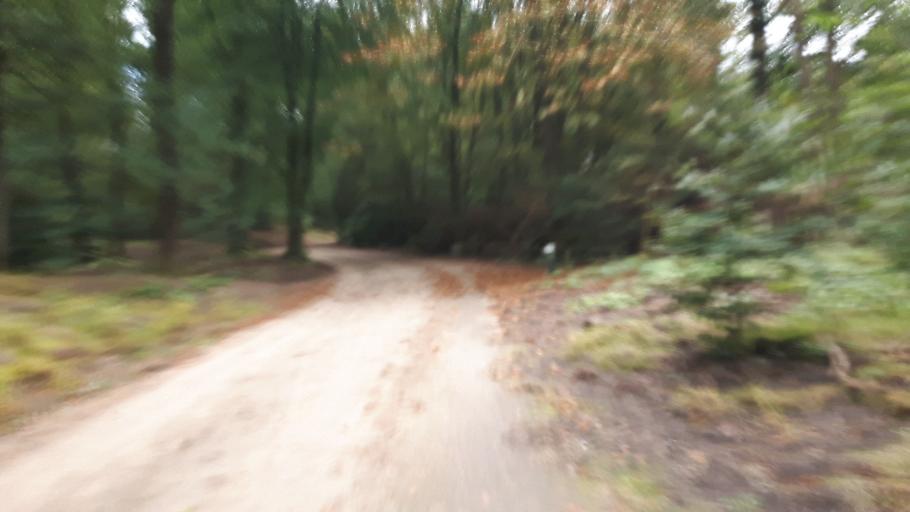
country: NL
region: Gelderland
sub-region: Gemeente Ermelo
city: Ermelo
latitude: 52.2714
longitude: 5.6401
